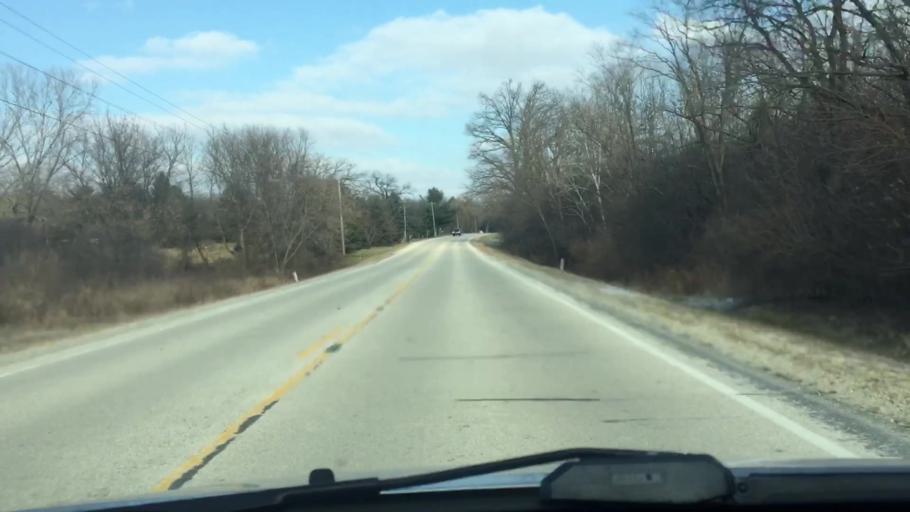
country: US
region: Wisconsin
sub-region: Jefferson County
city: Palmyra
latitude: 42.8940
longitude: -88.5536
